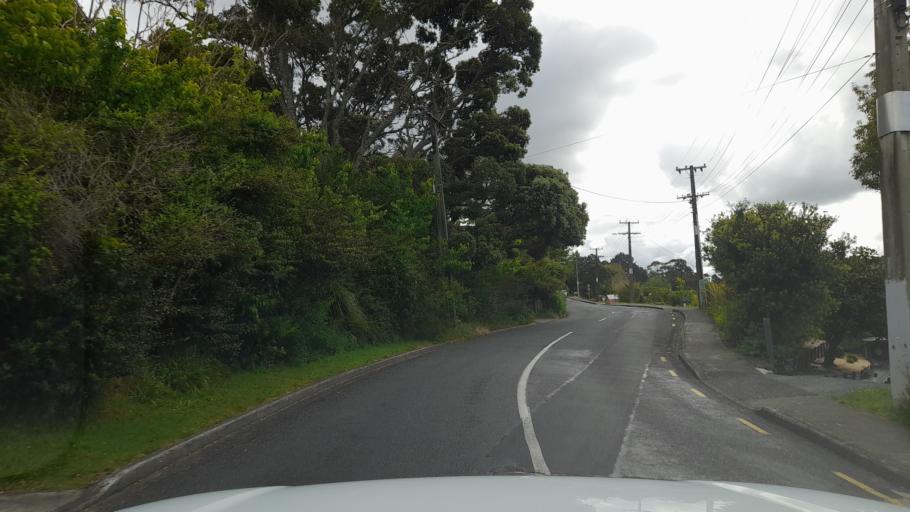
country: NZ
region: Northland
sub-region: Whangarei
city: Whangarei
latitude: -35.7393
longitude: 174.3208
